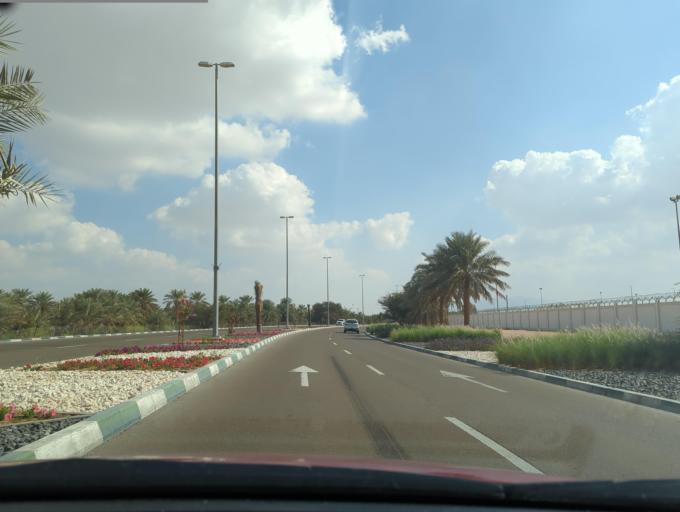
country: AE
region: Abu Dhabi
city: Al Ain
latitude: 24.1819
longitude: 55.6451
